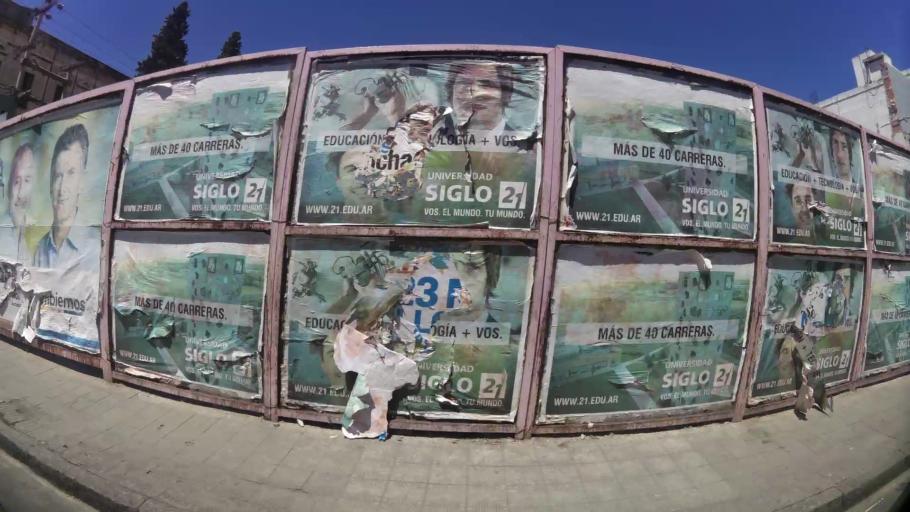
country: AR
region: Cordoba
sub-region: Departamento de Capital
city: Cordoba
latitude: -31.4127
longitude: -64.1996
